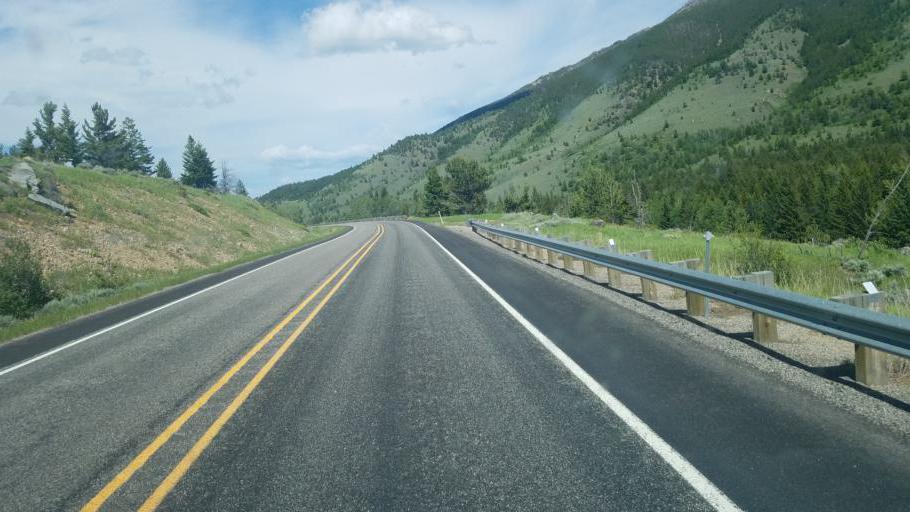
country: US
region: Montana
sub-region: Carbon County
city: Red Lodge
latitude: 45.1007
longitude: -109.3115
